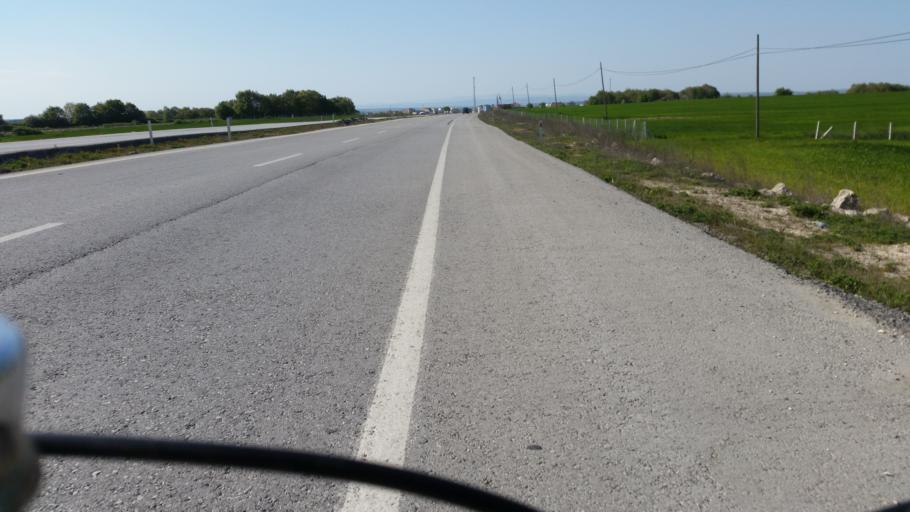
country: TR
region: Tekirdag
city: Cerkezkoey
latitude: 41.3450
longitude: 27.9619
